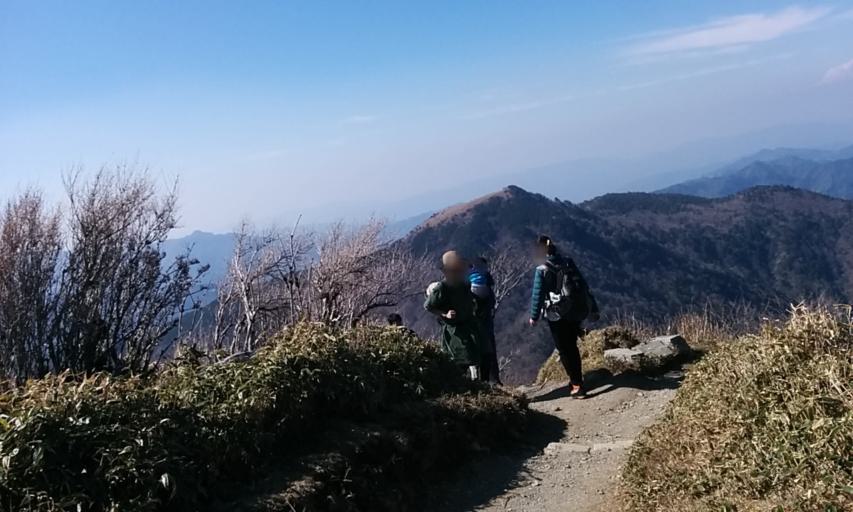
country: JP
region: Tokushima
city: Wakimachi
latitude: 33.8591
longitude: 134.0941
